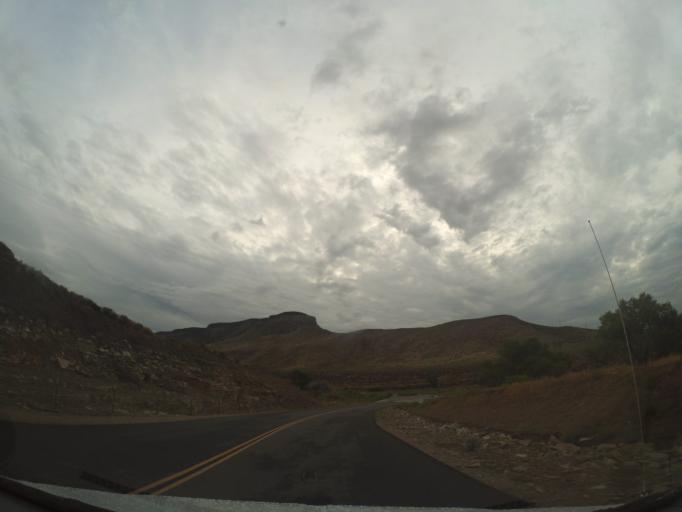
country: US
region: Utah
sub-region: Washington County
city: LaVerkin
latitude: 37.2050
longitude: -113.1726
